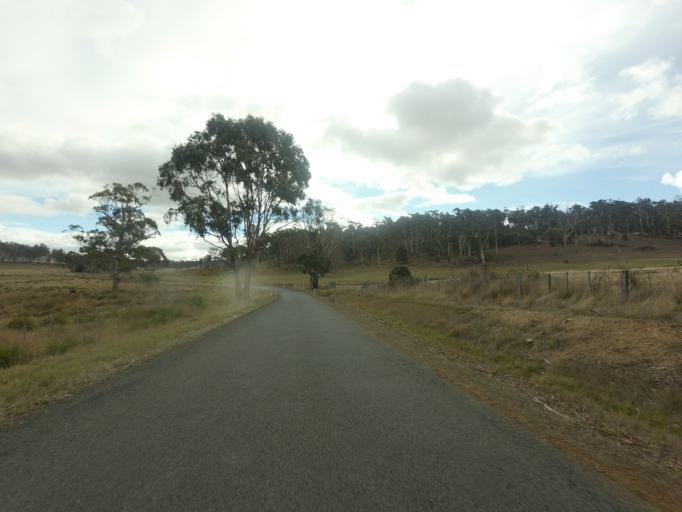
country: AU
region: Tasmania
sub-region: Brighton
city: Bridgewater
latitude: -42.3974
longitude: 147.3774
